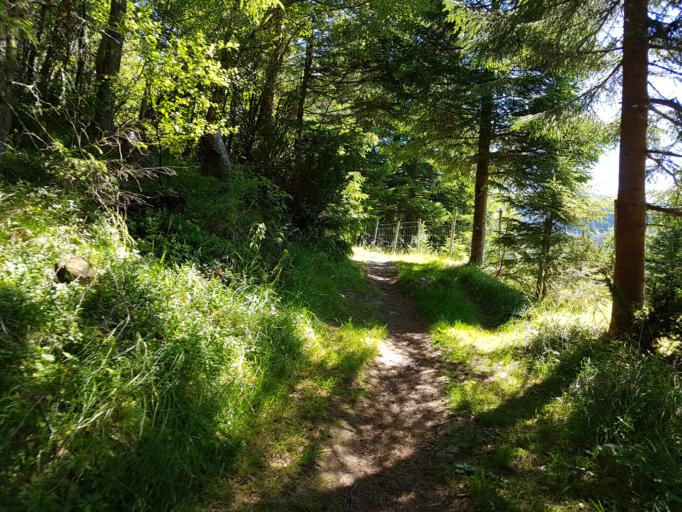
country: NO
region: Sor-Trondelag
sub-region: Skaun
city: Borsa
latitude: 63.4305
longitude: 10.1973
